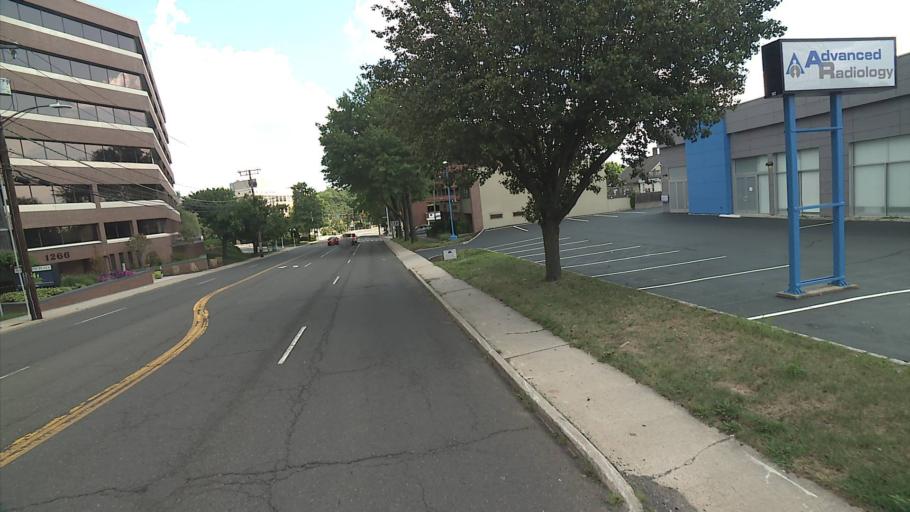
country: US
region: Connecticut
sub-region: Fairfield County
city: Stamford
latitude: 41.0598
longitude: -73.5096
